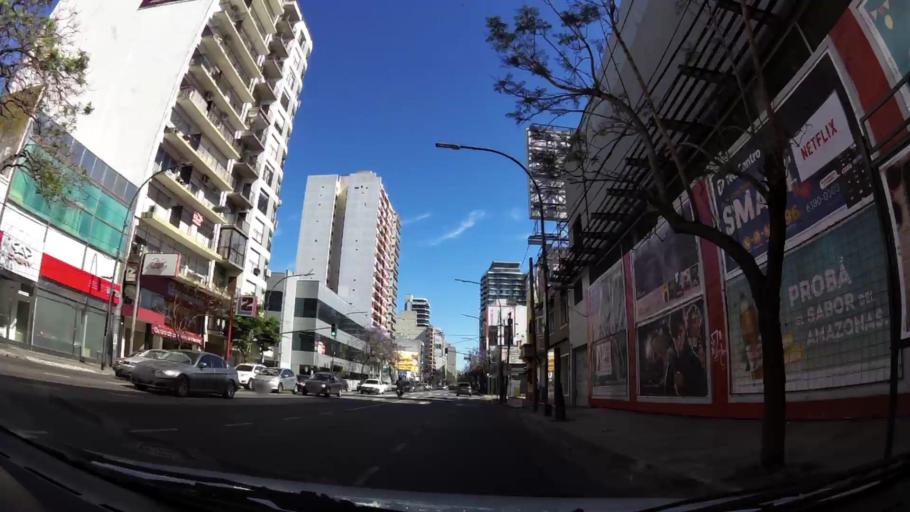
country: AR
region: Buenos Aires
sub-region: Partido de Vicente Lopez
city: Olivos
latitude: -34.5208
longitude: -58.4739
